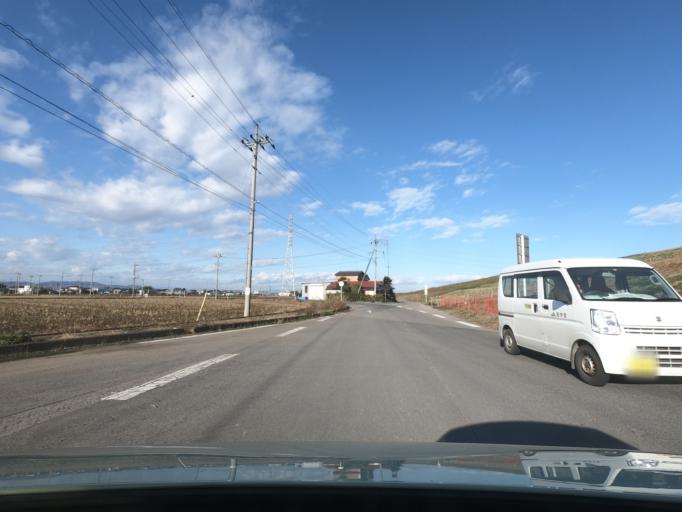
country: JP
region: Ibaraki
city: Koga
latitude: 36.2512
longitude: 139.7352
